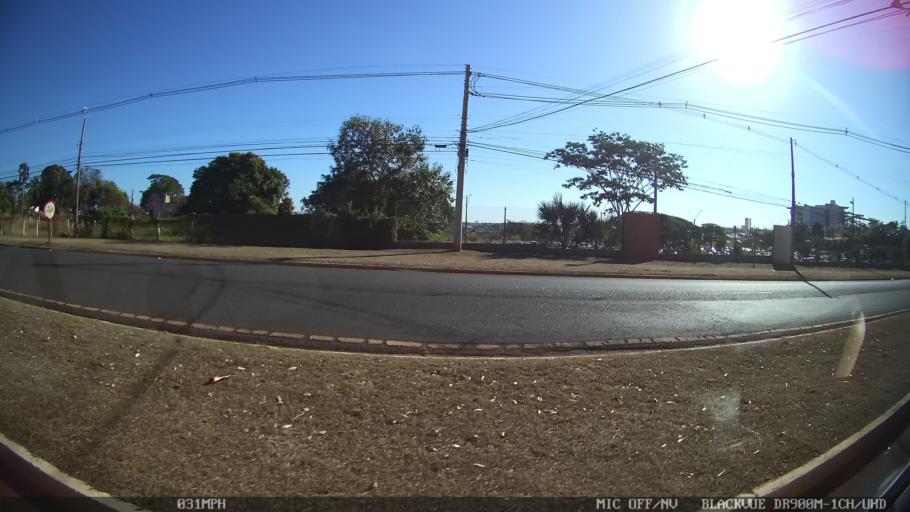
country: BR
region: Sao Paulo
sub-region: Olimpia
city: Olimpia
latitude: -20.7207
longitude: -48.9062
